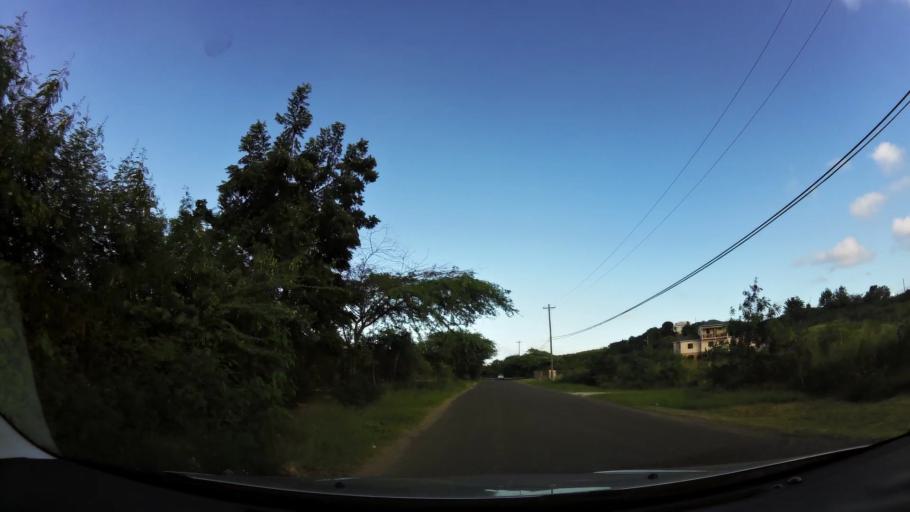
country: AG
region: Saint George
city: Piggotts
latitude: 17.1214
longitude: -61.7977
